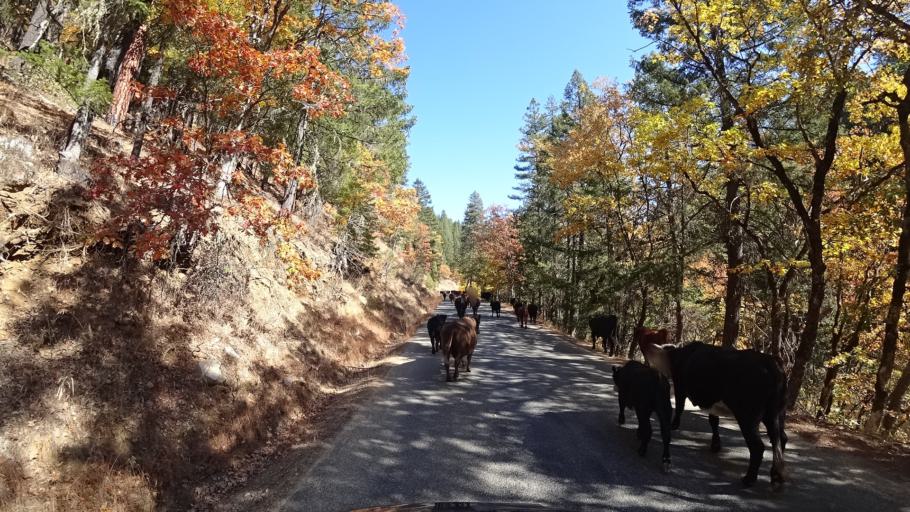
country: US
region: California
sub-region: Siskiyou County
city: Happy Camp
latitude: 41.6388
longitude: -123.0648
